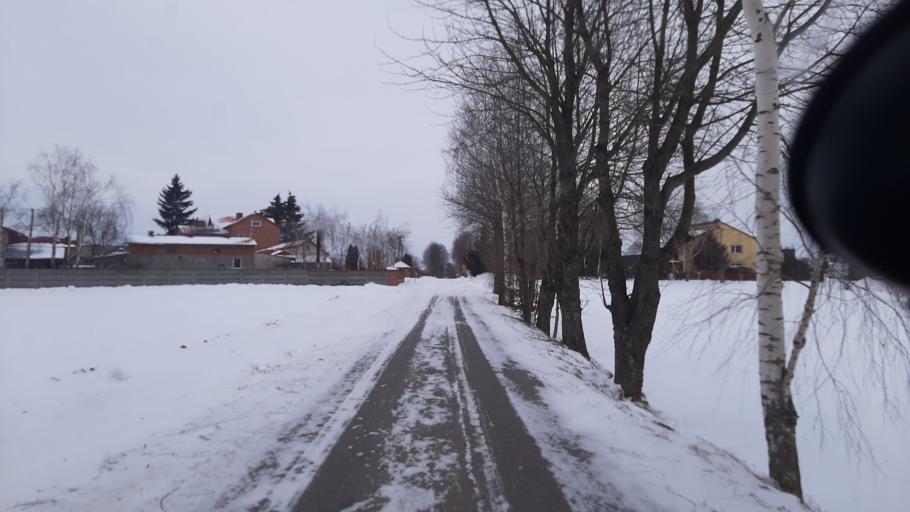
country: PL
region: Lublin Voivodeship
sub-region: Powiat lubelski
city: Garbow
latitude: 51.3298
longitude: 22.3002
